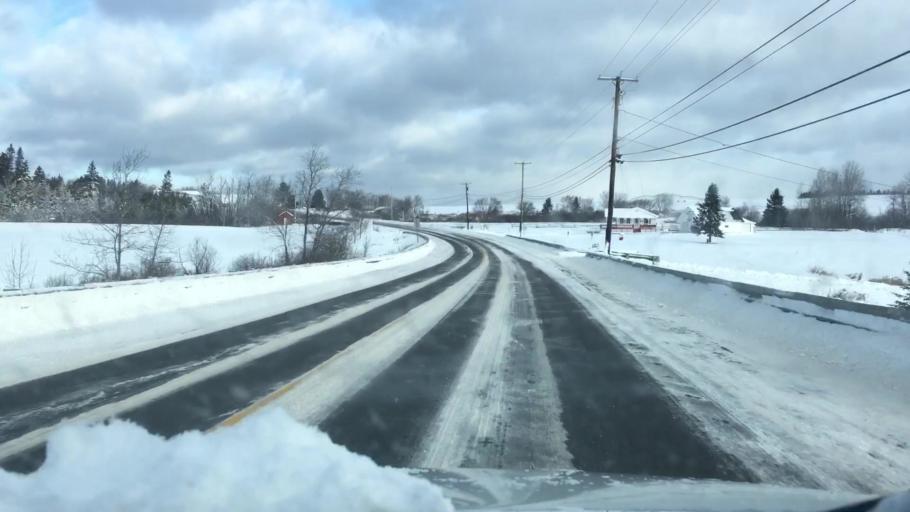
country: US
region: Maine
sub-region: Aroostook County
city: Caribou
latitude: 46.9462
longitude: -68.0228
